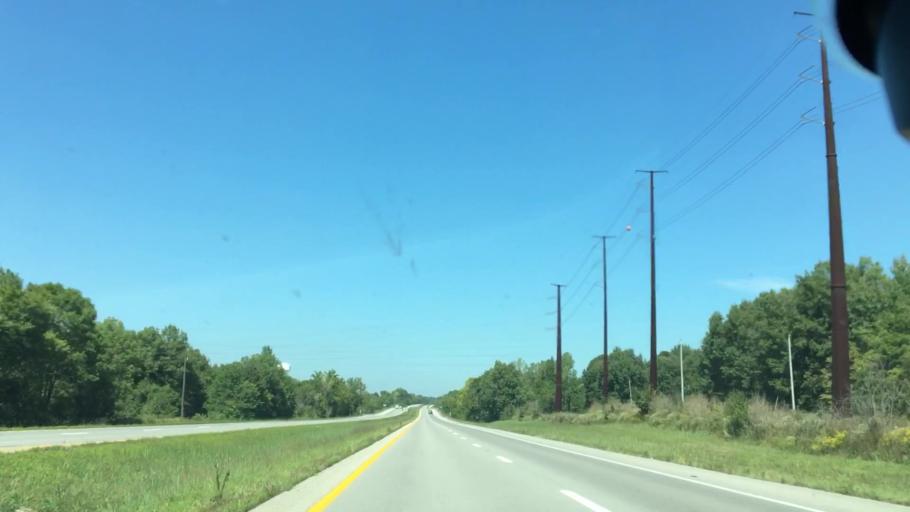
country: US
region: Kentucky
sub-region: Webster County
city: Sebree
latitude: 37.6416
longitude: -87.5106
